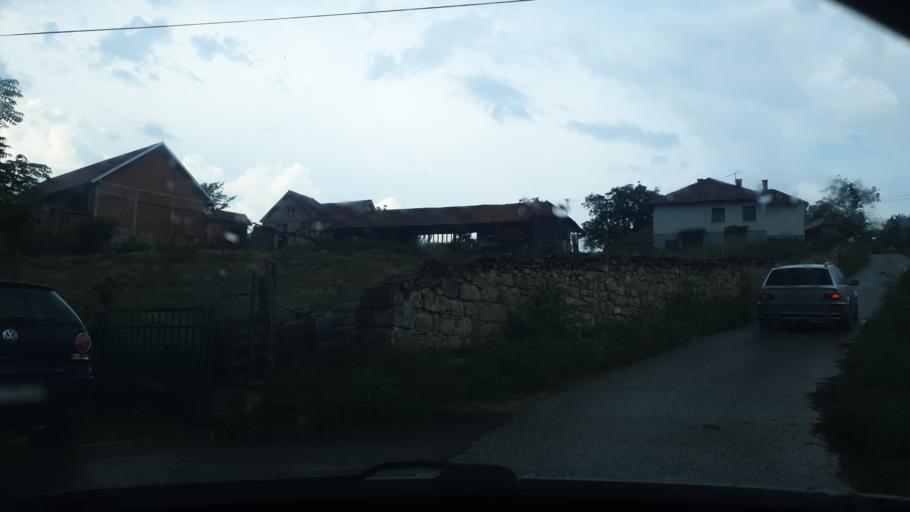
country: RS
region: Central Serbia
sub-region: Sumadijski Okrug
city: Kragujevac
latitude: 44.0813
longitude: 20.7979
